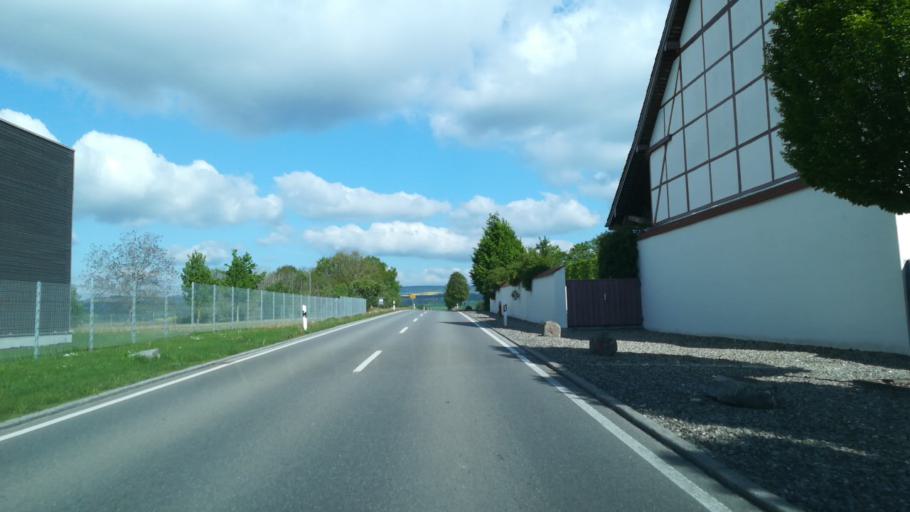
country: CH
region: Schaffhausen
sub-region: Bezirk Reiat
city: Thayngen
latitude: 47.7769
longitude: 8.7237
